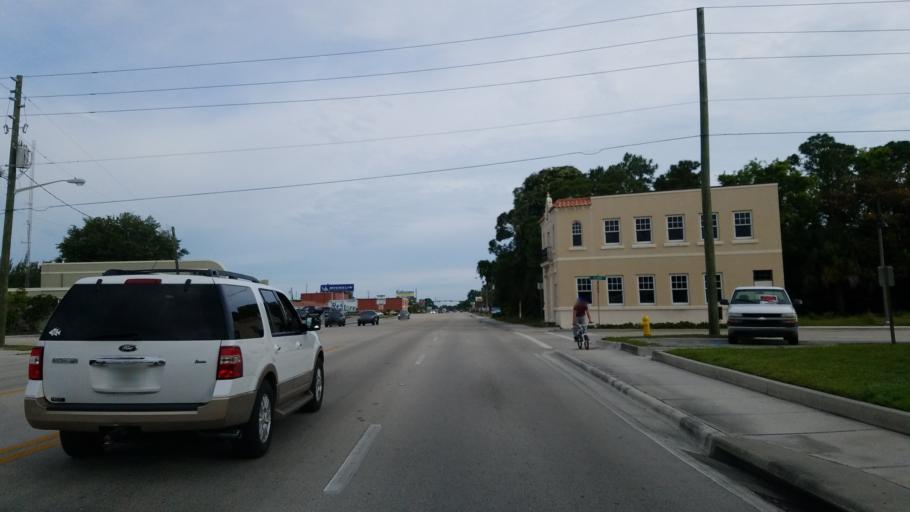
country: US
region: Florida
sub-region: Martin County
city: Port Salerno
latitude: 27.1651
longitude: -80.2189
